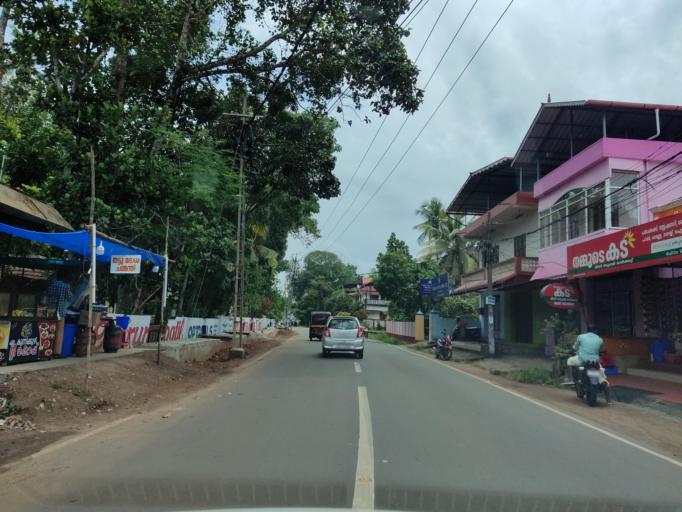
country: IN
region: Kerala
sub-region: Pattanamtitta
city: Adur
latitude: 9.2297
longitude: 76.6641
